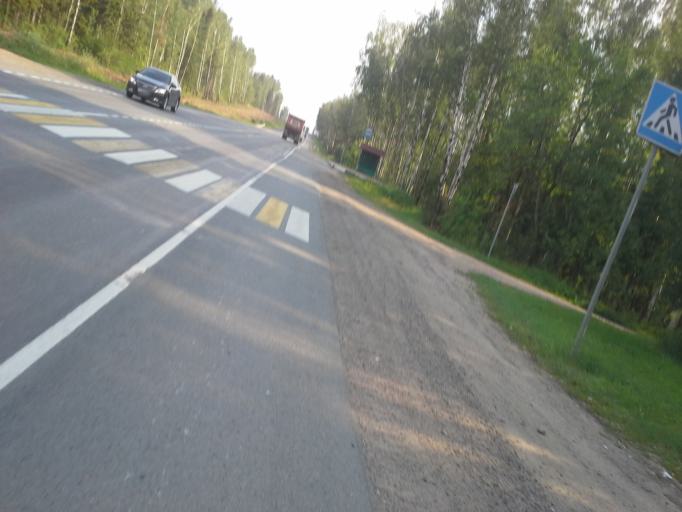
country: RU
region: Moskovskaya
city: Snegiri
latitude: 55.8883
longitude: 36.9439
